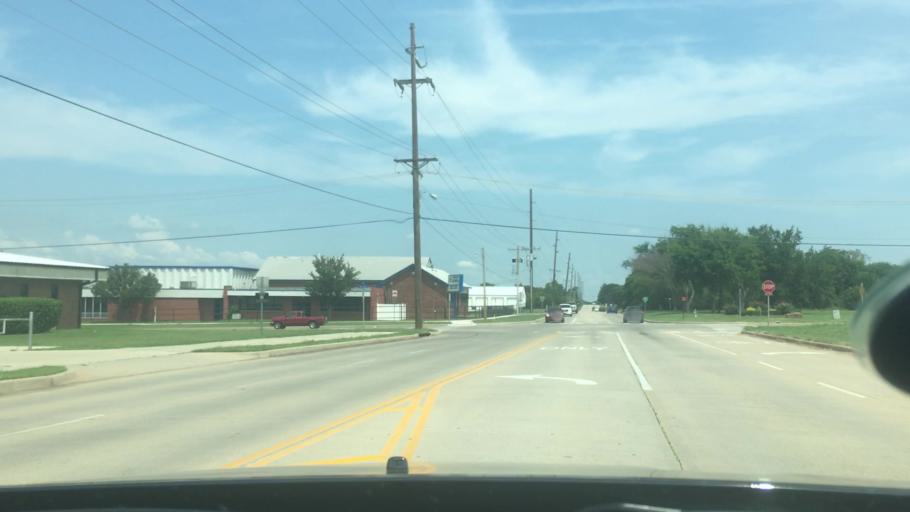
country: US
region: Oklahoma
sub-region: Pottawatomie County
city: Shawnee
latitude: 35.3610
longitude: -96.8943
